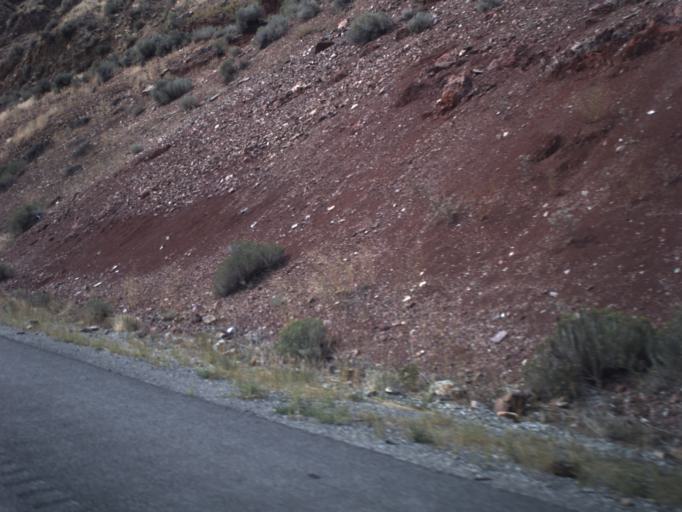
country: US
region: Utah
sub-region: Salt Lake County
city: East Millcreek
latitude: 40.7119
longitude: -111.7921
